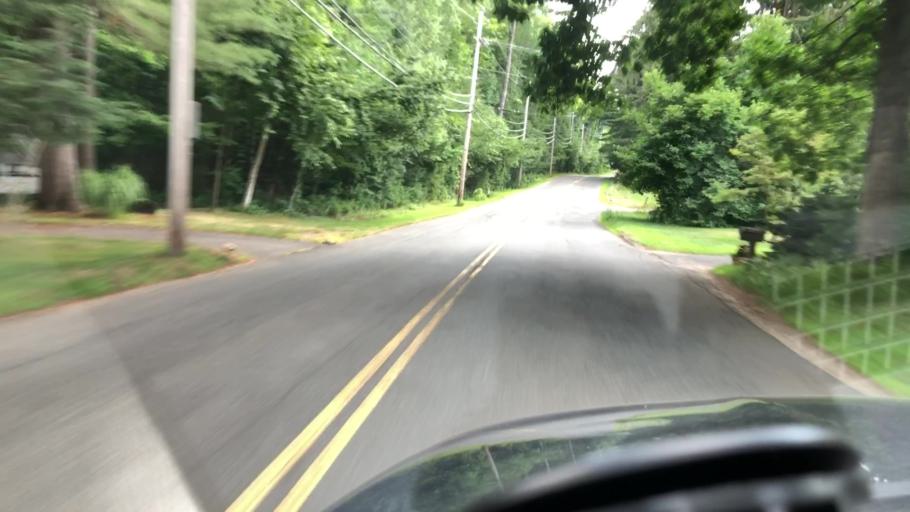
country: US
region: Massachusetts
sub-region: Hampden County
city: Holyoke
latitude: 42.1867
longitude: -72.6780
